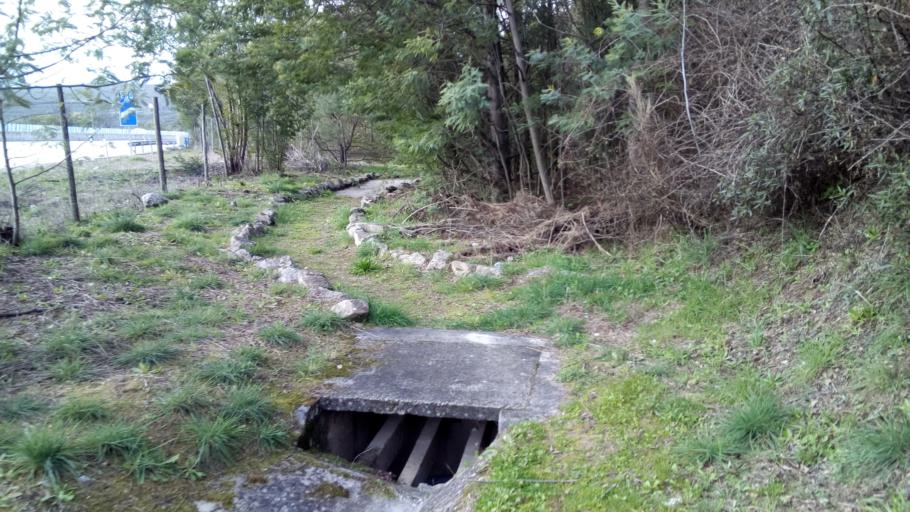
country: PT
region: Guarda
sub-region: Fornos de Algodres
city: Fornos de Algodres
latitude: 40.6114
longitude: -7.5294
